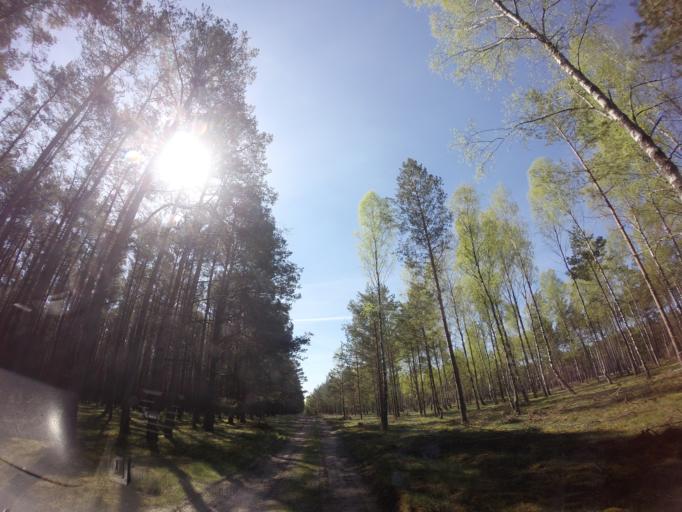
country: PL
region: West Pomeranian Voivodeship
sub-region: Powiat drawski
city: Kalisz Pomorski
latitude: 53.1991
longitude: 15.9386
